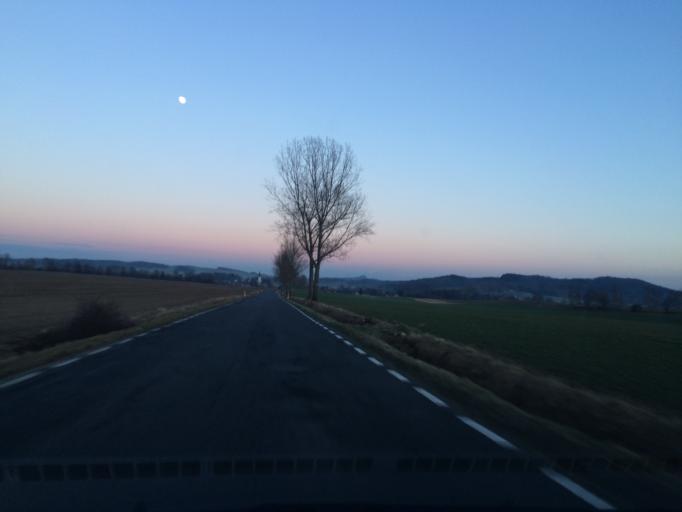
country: PL
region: Lower Silesian Voivodeship
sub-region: Powiat zlotoryjski
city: Olszanica
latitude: 51.1202
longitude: 15.7926
